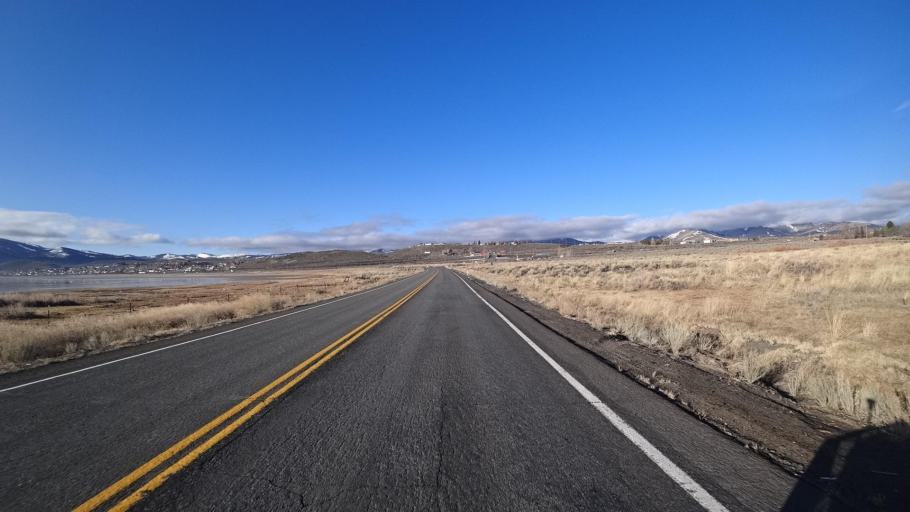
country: US
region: Nevada
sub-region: Washoe County
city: Cold Springs
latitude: 39.6711
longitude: -119.9907
